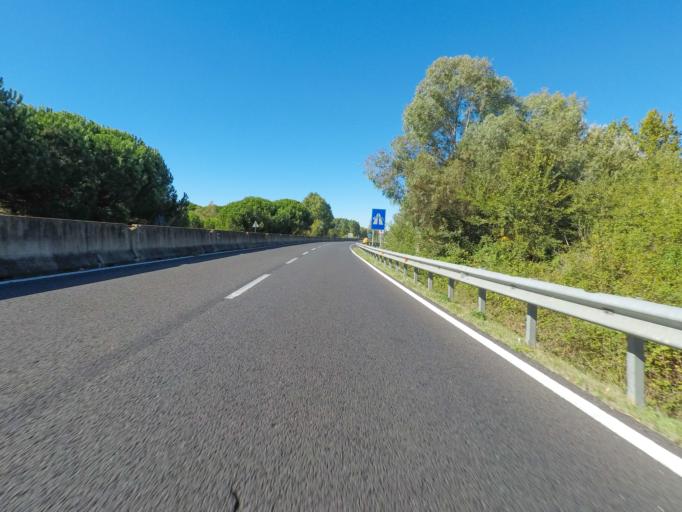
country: IT
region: Tuscany
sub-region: Provincia di Grosseto
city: Albinia
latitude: 42.4807
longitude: 11.2220
